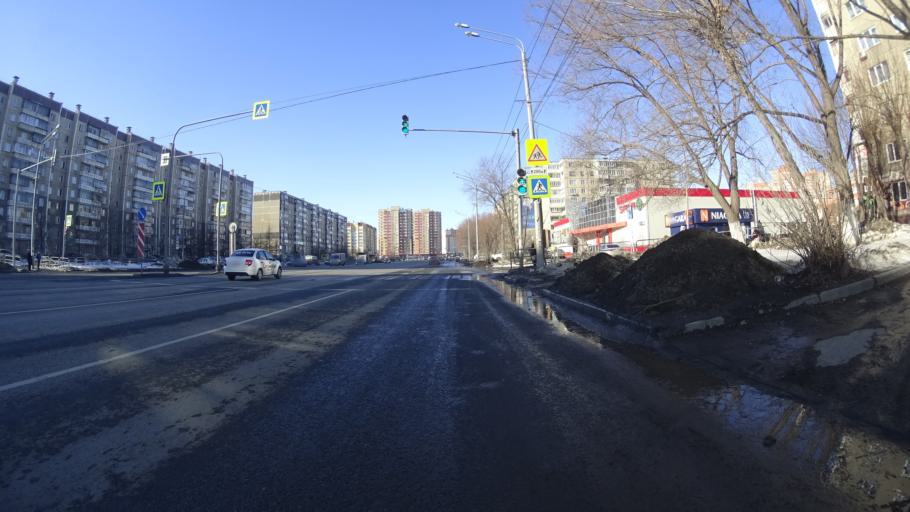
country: RU
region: Chelyabinsk
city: Roshchino
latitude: 55.1891
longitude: 61.2839
